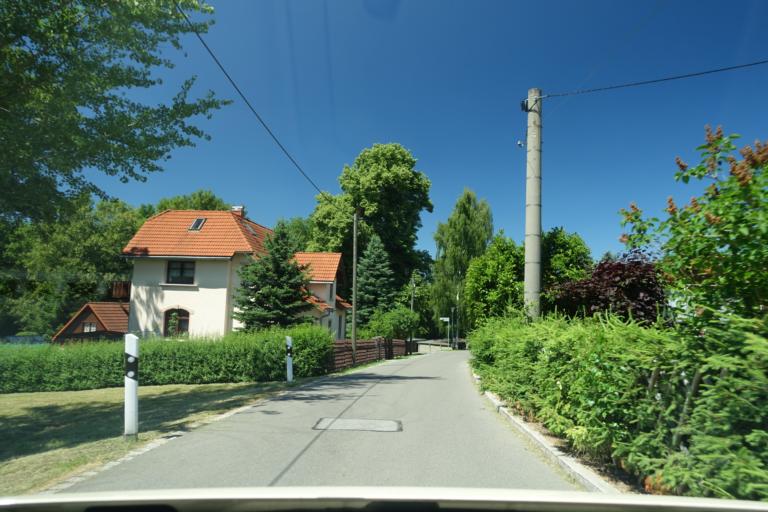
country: DE
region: Saxony
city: Eppendorf
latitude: 50.8011
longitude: 13.2214
